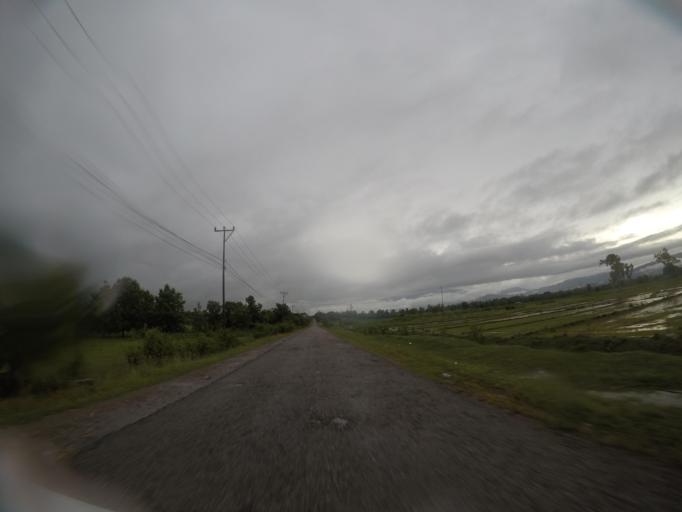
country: TL
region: Bobonaro
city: Maliana
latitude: -8.9705
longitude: 125.1313
